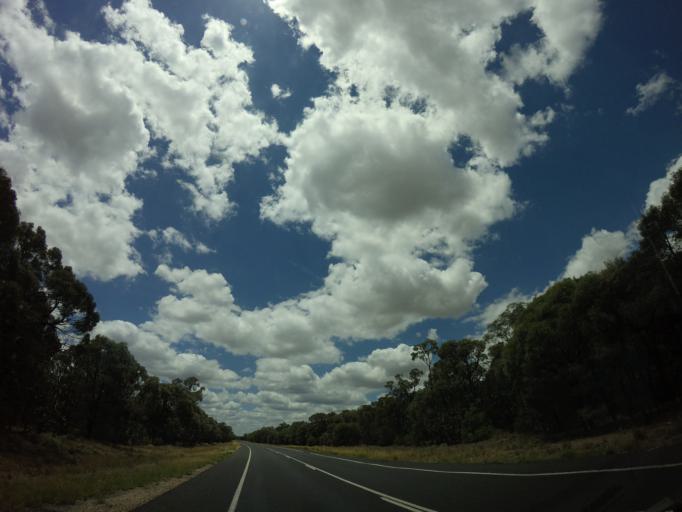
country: AU
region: Queensland
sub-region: Goondiwindi
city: Goondiwindi
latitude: -28.1064
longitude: 150.7213
